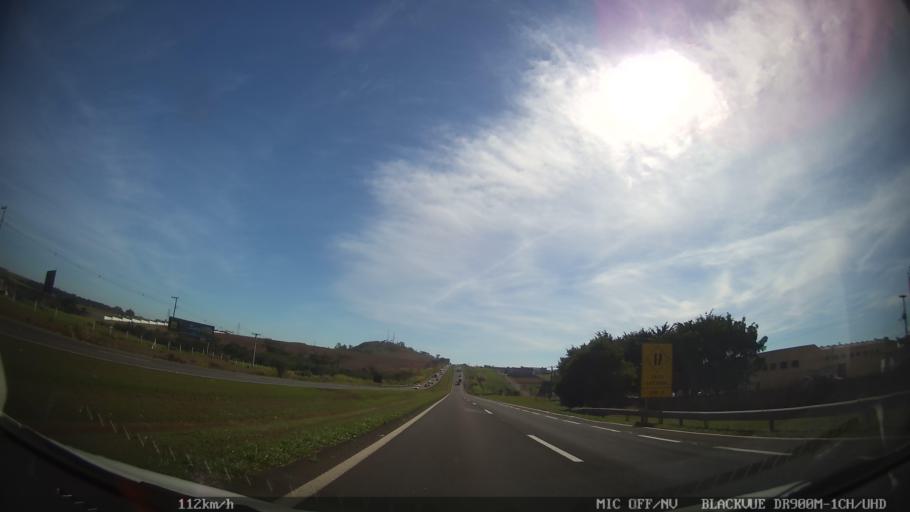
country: BR
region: Sao Paulo
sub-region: Leme
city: Leme
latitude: -22.1721
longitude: -47.3988
